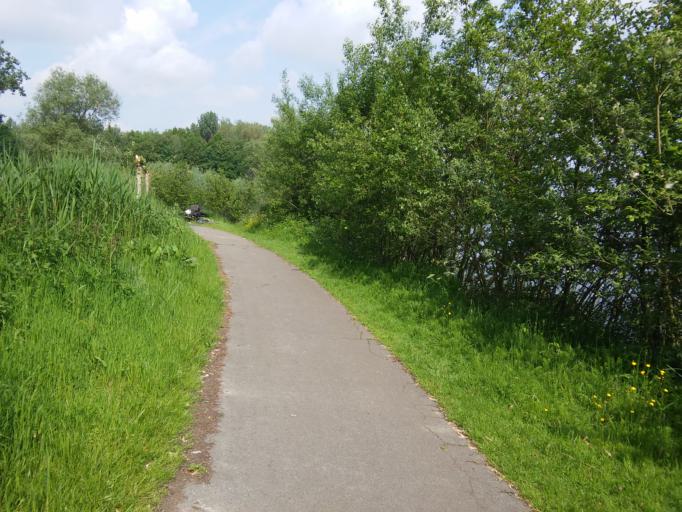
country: BE
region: Flanders
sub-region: Provincie Vlaams-Brabant
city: Zemst
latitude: 51.0042
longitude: 4.4497
